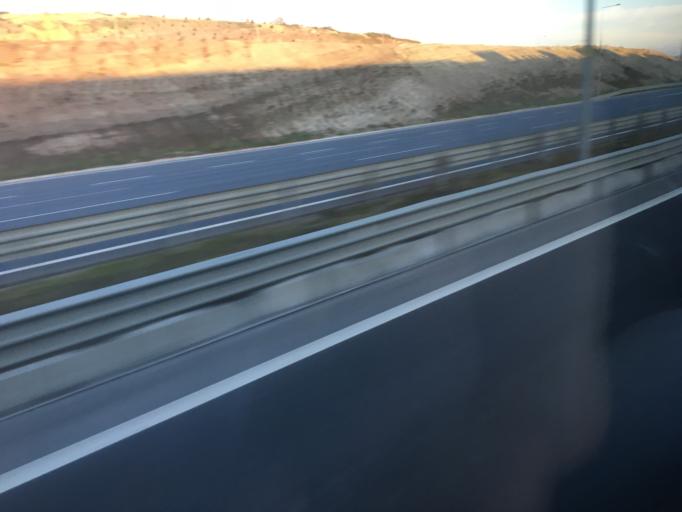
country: TR
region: Istanbul
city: Mahmut Sevket Pasa
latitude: 41.1180
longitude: 29.2884
